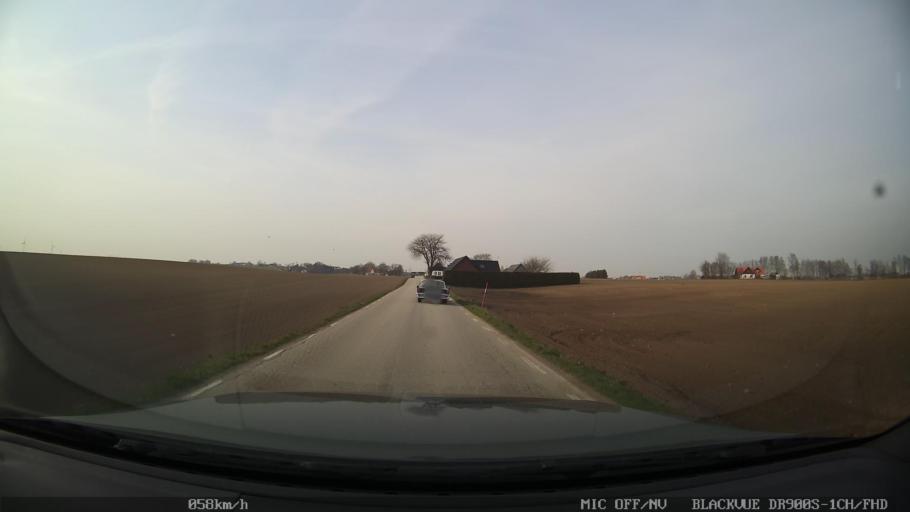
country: SE
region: Skane
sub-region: Ystads Kommun
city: Ystad
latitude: 55.4591
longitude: 13.8267
